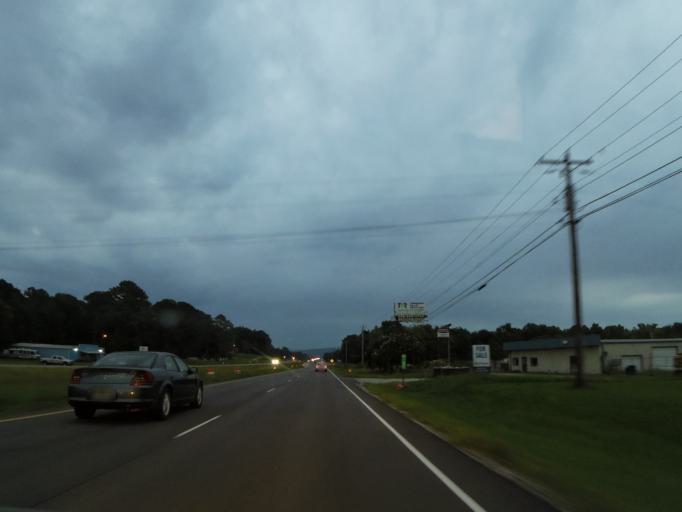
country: US
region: Alabama
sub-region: Madison County
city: Moores Mill
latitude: 34.7512
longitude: -86.4607
